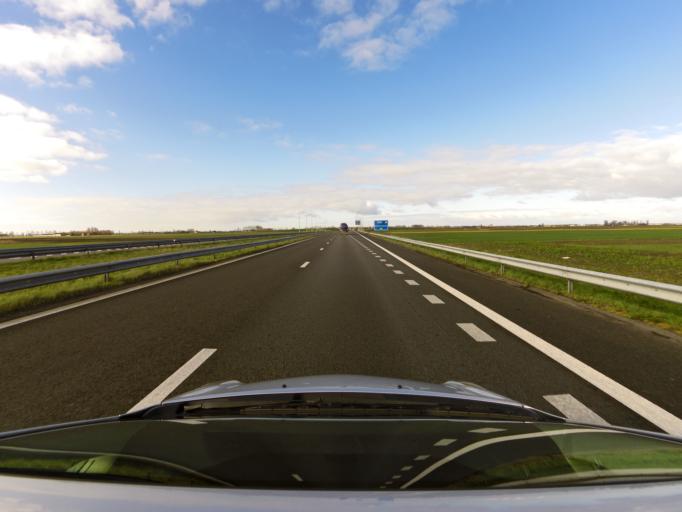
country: BE
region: Flanders
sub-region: Provincie West-Vlaanderen
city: Nieuwpoort
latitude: 51.0849
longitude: 2.7214
